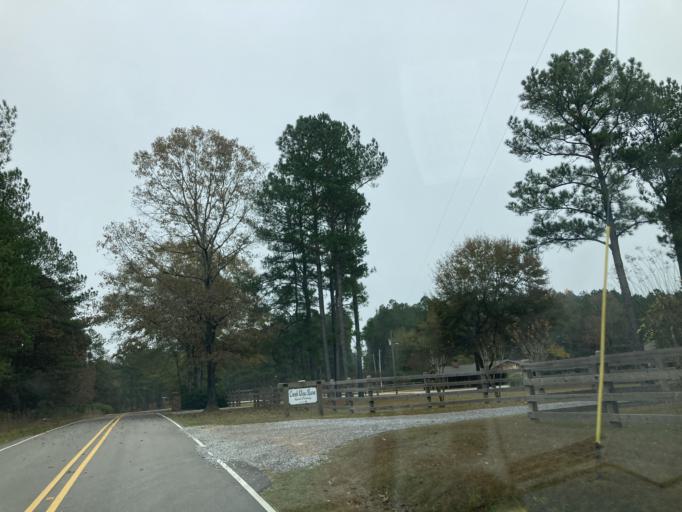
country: US
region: Mississippi
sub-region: Lamar County
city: Purvis
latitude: 31.0687
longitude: -89.4053
